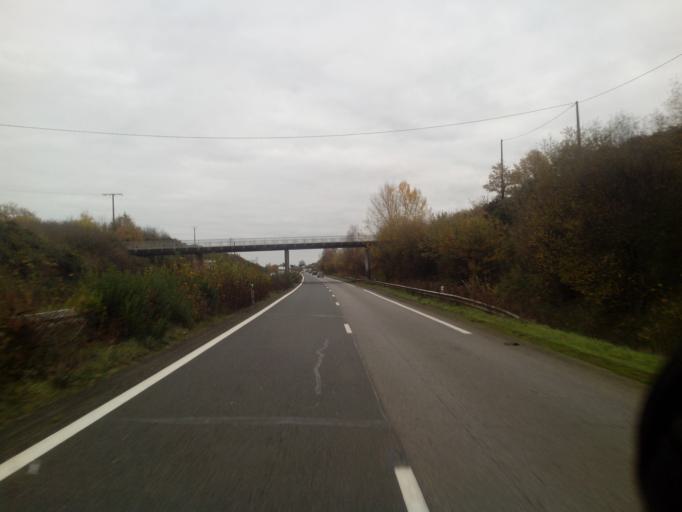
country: FR
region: Pays de la Loire
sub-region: Departement de la Loire-Atlantique
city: Vallet
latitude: 47.1550
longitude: -1.2599
